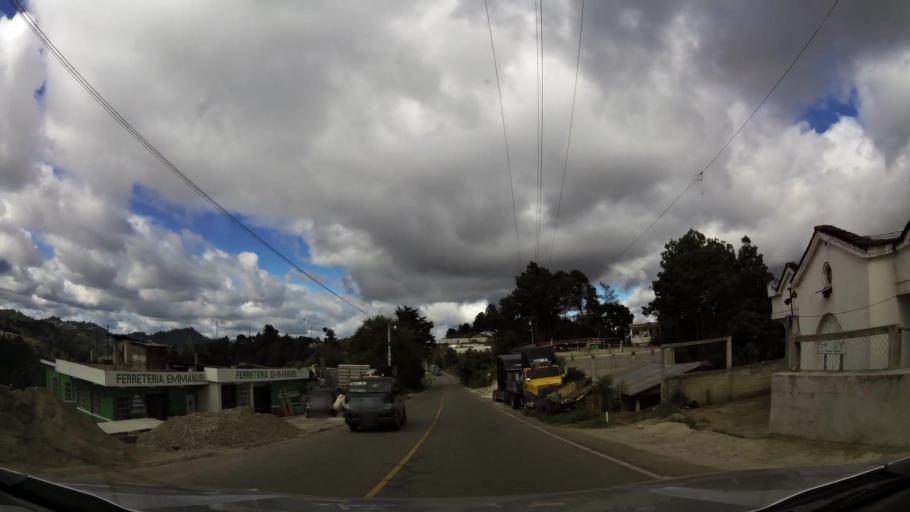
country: GT
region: Quiche
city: Chichicastenango
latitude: 14.8861
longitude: -91.1213
